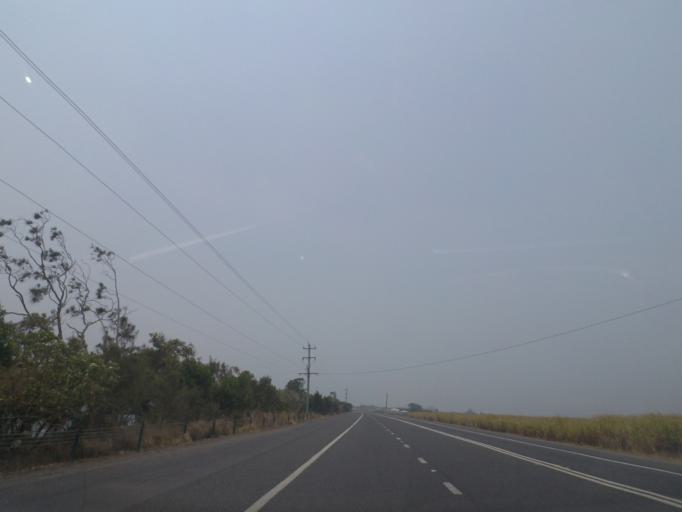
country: AU
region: New South Wales
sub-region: Richmond Valley
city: Evans Head
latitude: -28.9962
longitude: 153.4539
